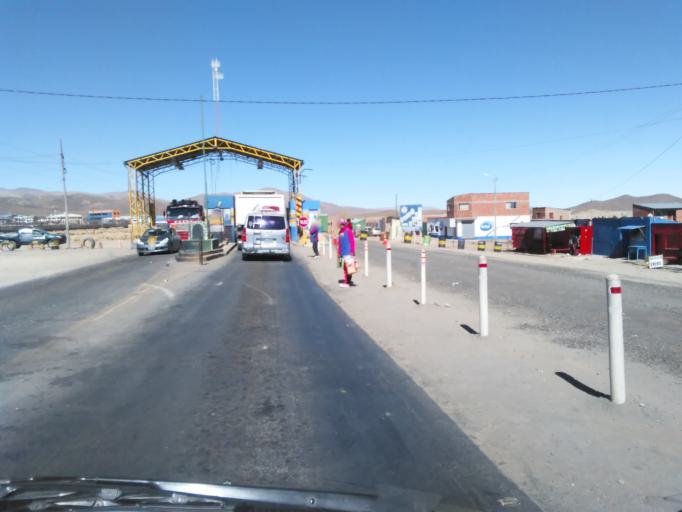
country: BO
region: Oruro
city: Oruro
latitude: -18.0180
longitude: -67.0313
